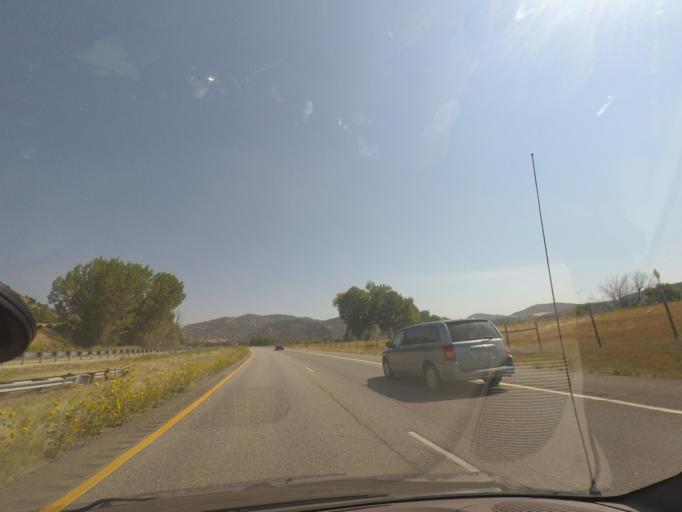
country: US
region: Colorado
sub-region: Garfield County
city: New Castle
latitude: 39.5567
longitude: -107.5628
